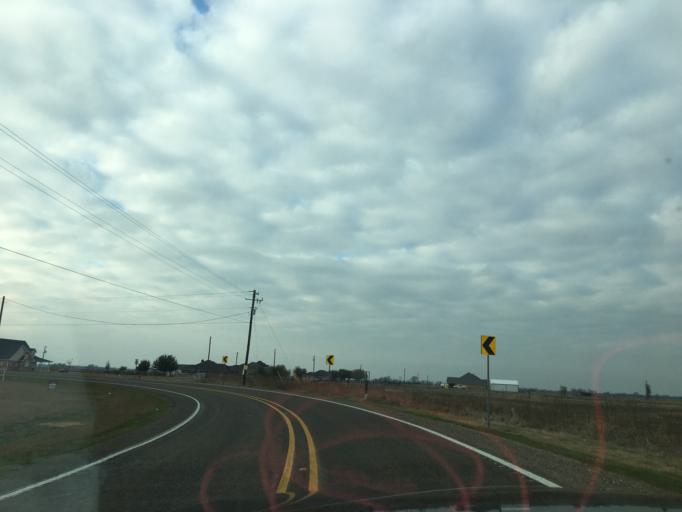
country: US
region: Texas
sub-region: Ellis County
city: Palmer
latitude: 32.4492
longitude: -96.7059
